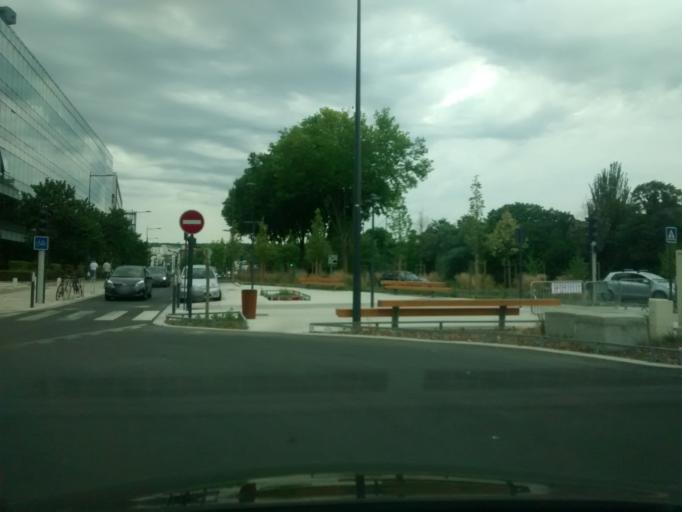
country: FR
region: Ile-de-France
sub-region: Departement des Hauts-de-Seine
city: Boulogne-Billancourt
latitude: 48.8273
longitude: 2.2609
